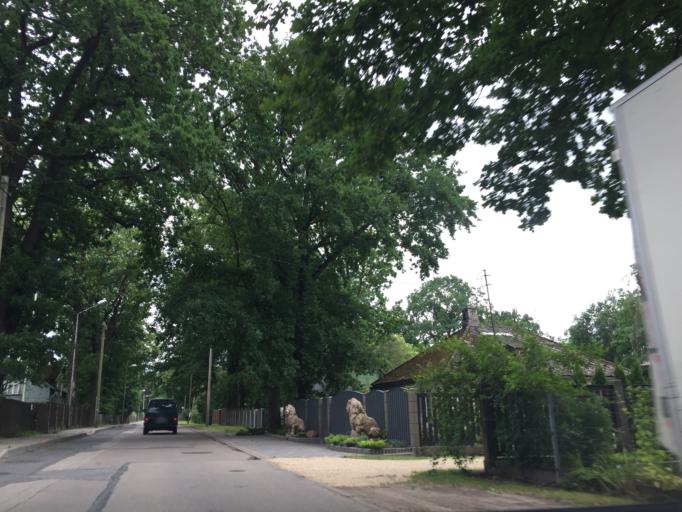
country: LV
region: Marupe
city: Marupe
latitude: 56.9386
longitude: 24.0318
